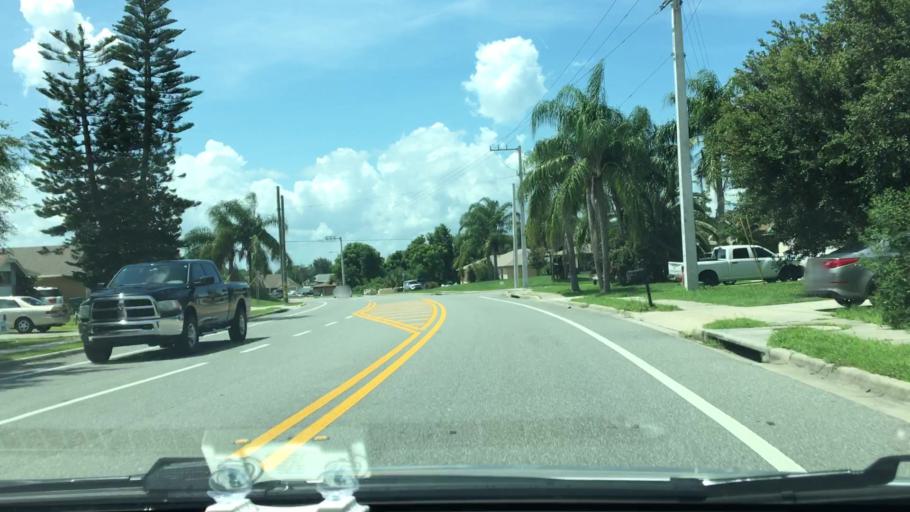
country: US
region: Florida
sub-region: Volusia County
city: Deltona
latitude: 28.8881
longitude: -81.2101
